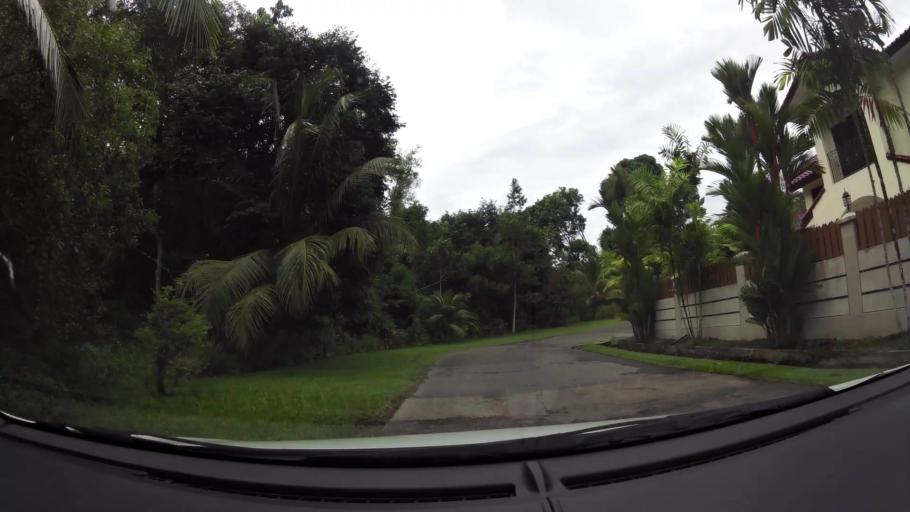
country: BN
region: Brunei and Muara
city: Bandar Seri Begawan
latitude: 4.8874
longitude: 114.9249
